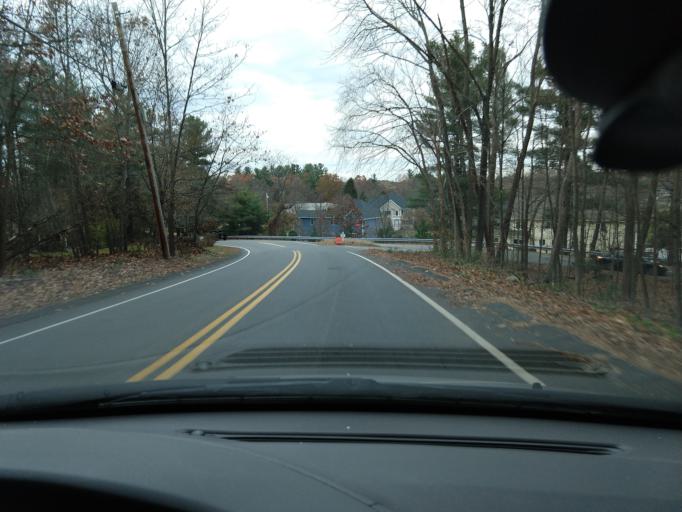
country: US
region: Massachusetts
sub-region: Middlesex County
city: Westford
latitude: 42.5932
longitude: -71.4316
